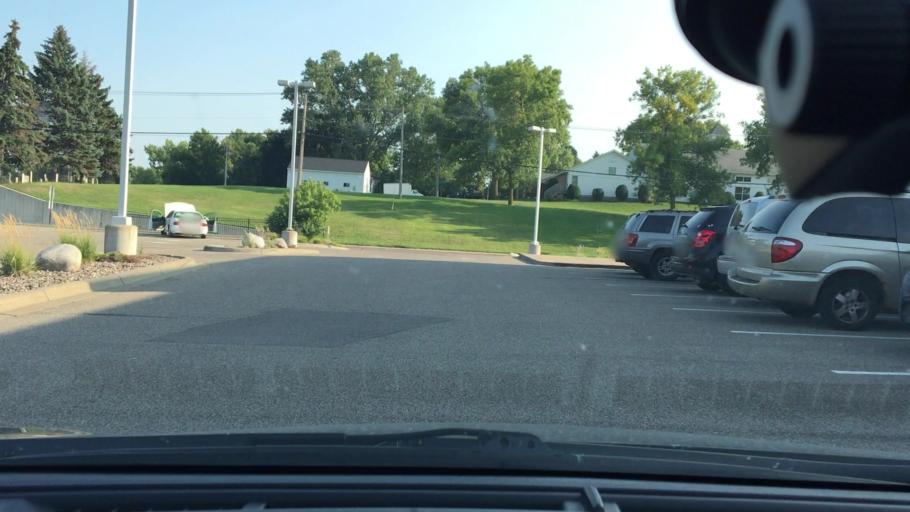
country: US
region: Minnesota
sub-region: Hennepin County
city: New Hope
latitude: 45.0079
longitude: -93.3814
